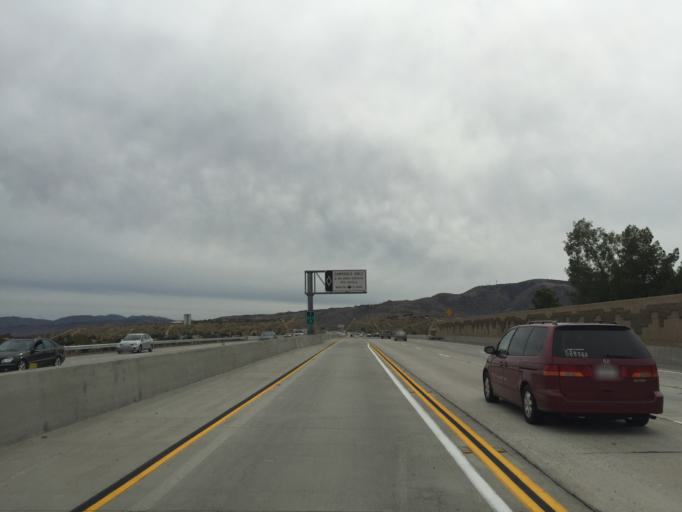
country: US
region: California
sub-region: Los Angeles County
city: Palmdale
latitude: 34.5735
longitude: -118.1336
